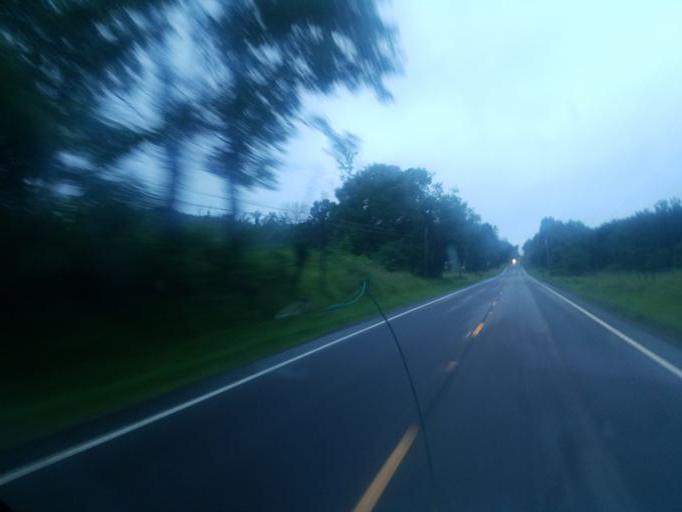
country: US
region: Ohio
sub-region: Carroll County
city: Carrollton
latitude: 40.5407
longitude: -81.0311
